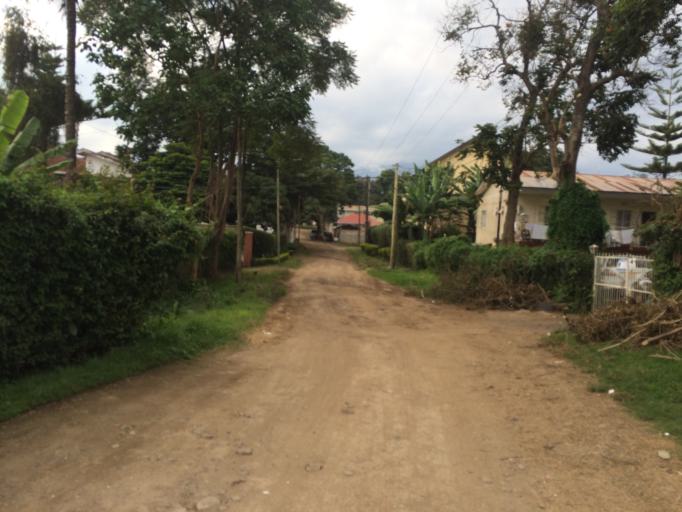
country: TZ
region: Arusha
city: Arusha
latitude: -3.3653
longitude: 36.6980
